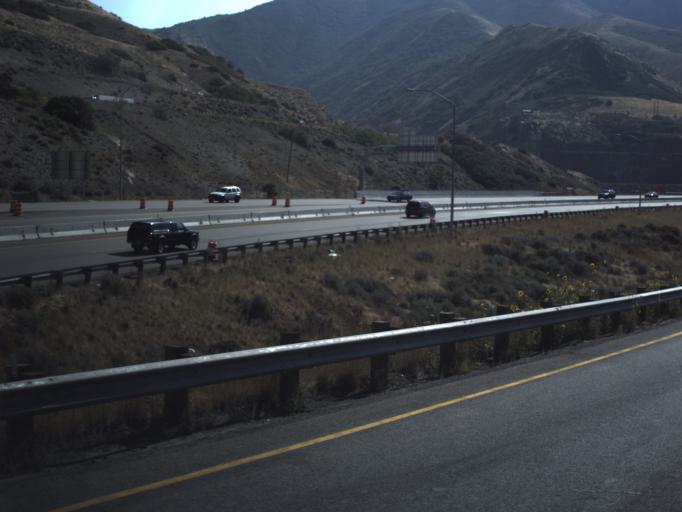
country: US
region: Utah
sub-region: Salt Lake County
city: East Millcreek
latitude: 40.7113
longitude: -111.8036
